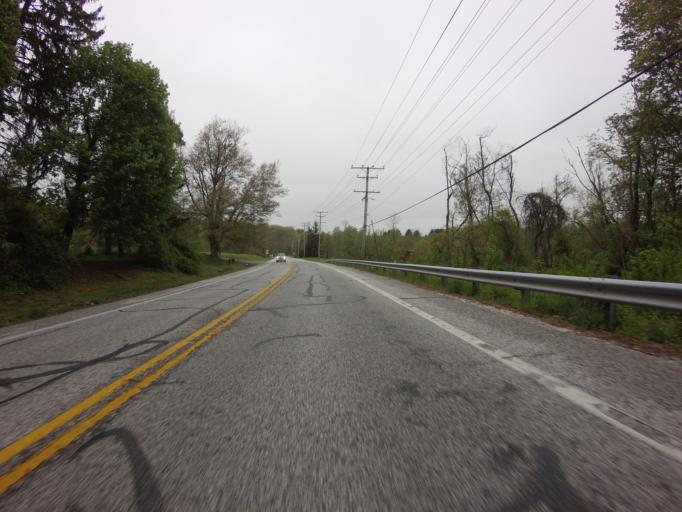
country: US
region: Maryland
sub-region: Baltimore County
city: Hunt Valley
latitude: 39.5838
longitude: -76.6633
